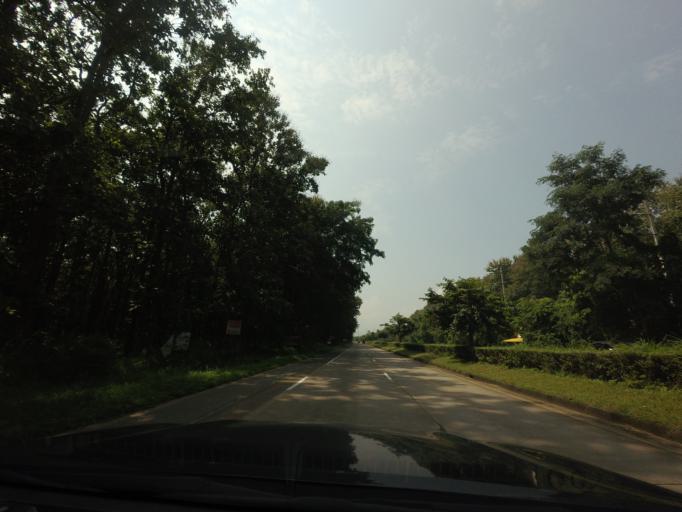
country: TH
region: Phrae
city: Den Chai
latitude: 17.9982
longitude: 100.1019
